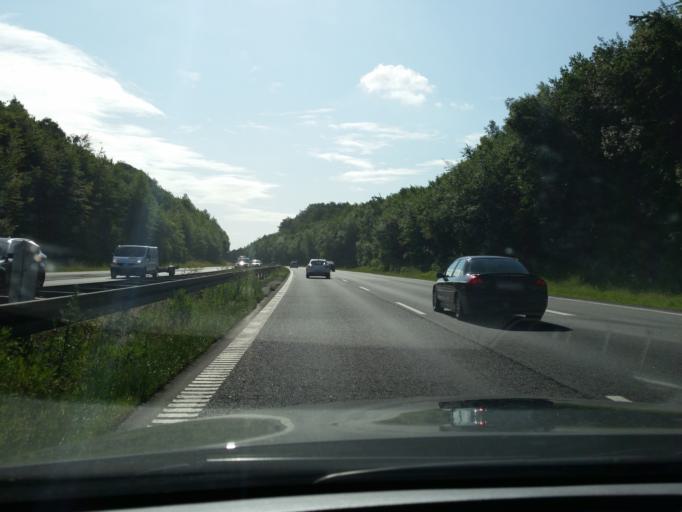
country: DK
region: South Denmark
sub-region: Assens Kommune
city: Tommerup Stationsby
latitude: 55.3868
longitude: 10.2163
